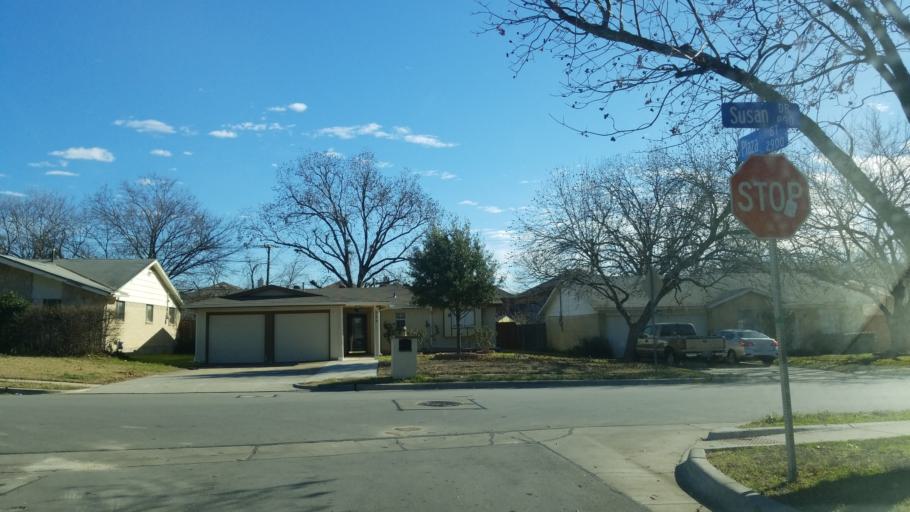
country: US
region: Texas
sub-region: Tarrant County
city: Arlington
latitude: 32.7276
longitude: -97.0574
